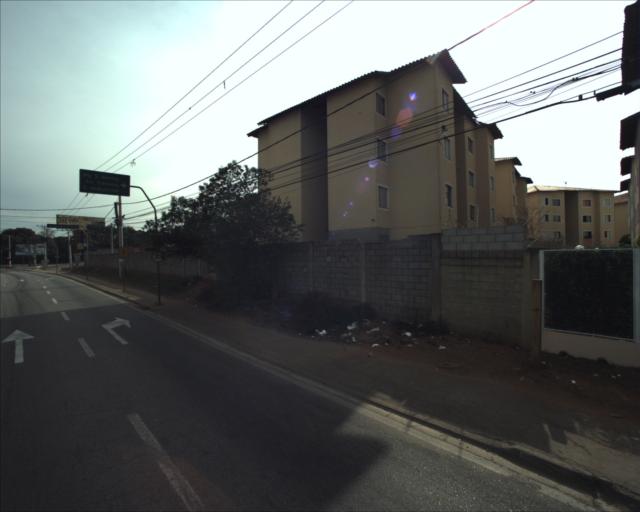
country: BR
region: Sao Paulo
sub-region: Sorocaba
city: Sorocaba
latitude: -23.4550
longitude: -47.5054
